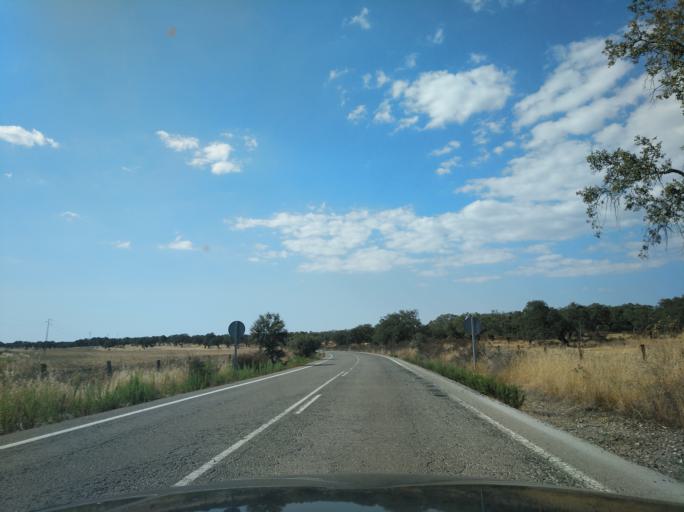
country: ES
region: Andalusia
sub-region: Provincia de Huelva
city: Santa Barbara de Casa
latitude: 37.7644
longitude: -7.1372
